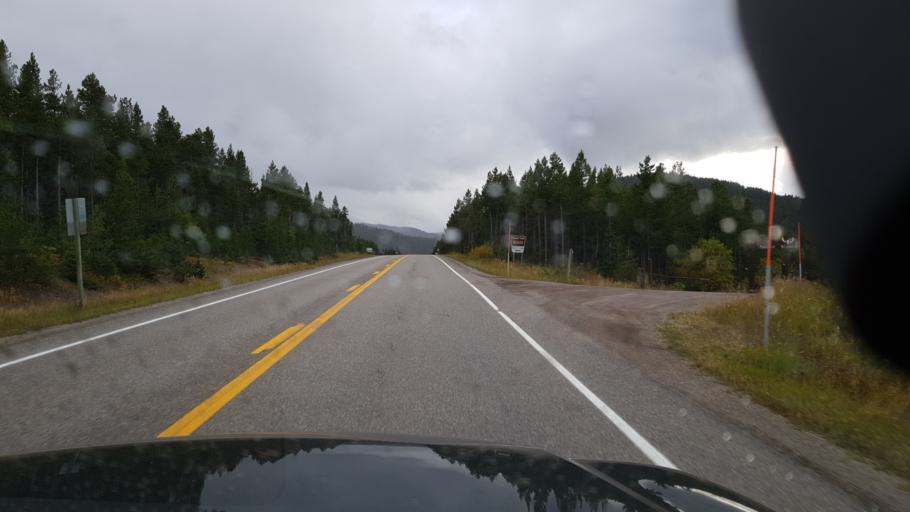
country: US
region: Montana
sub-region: Glacier County
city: South Browning
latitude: 48.3138
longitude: -113.3576
